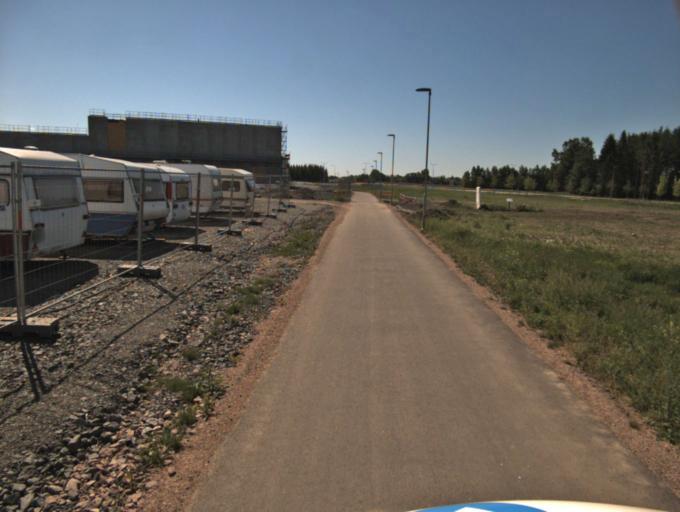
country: SE
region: Skane
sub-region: Kristianstads Kommun
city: Kristianstad
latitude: 56.0257
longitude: 14.1918
